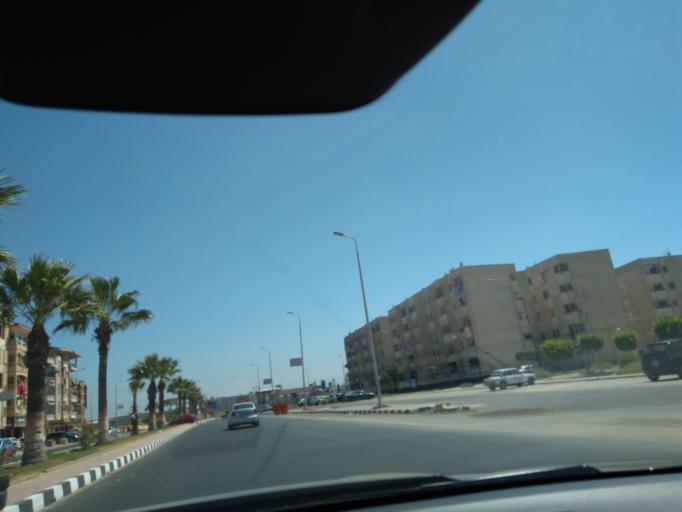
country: EG
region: Dumyat
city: Faraskur
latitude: 31.4263
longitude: 31.6748
